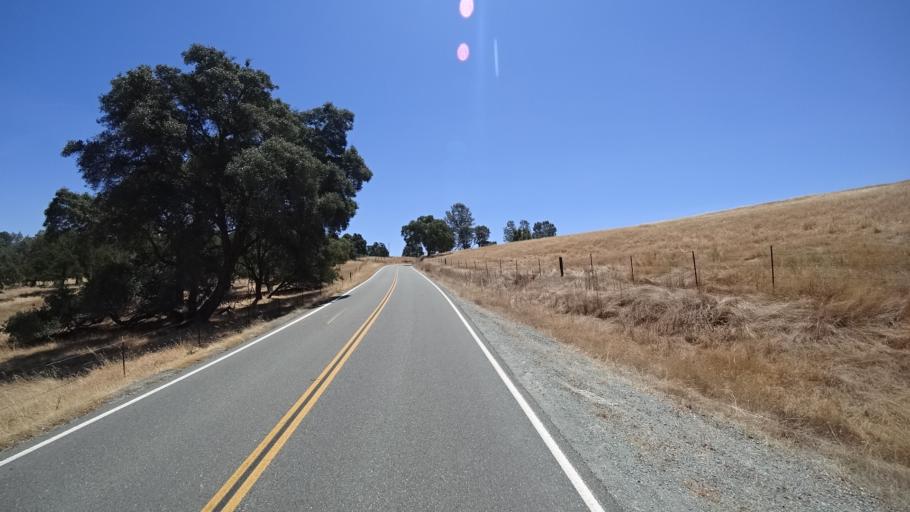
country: US
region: California
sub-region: Calaveras County
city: Valley Springs
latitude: 38.2275
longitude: -120.8364
